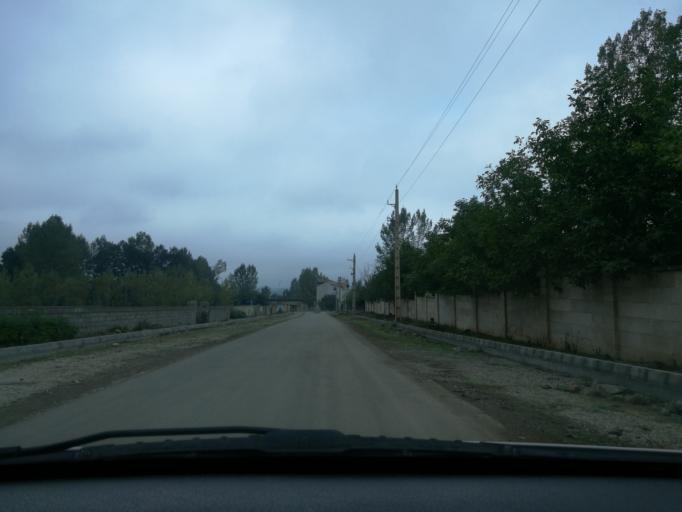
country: IR
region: Mazandaran
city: `Abbasabad
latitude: 36.5002
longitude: 51.2150
